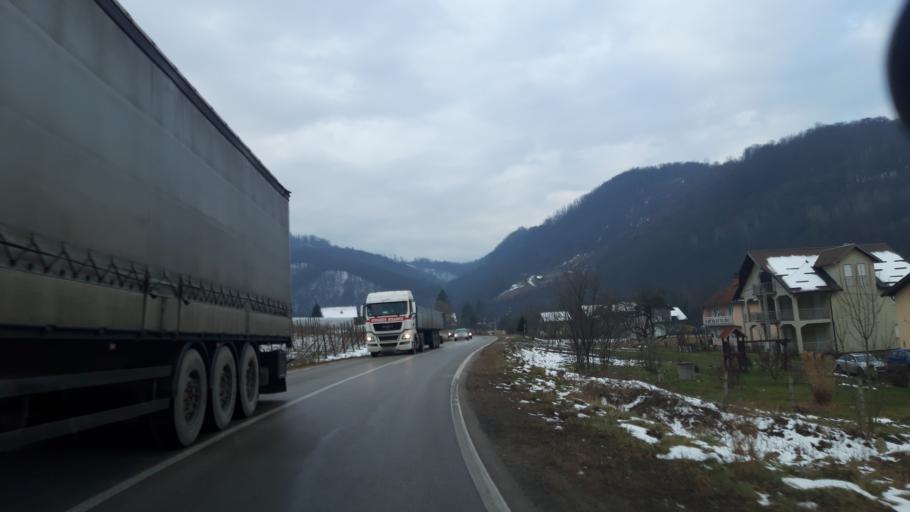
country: BA
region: Republika Srpska
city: Milici
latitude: 44.2282
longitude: 19.1049
